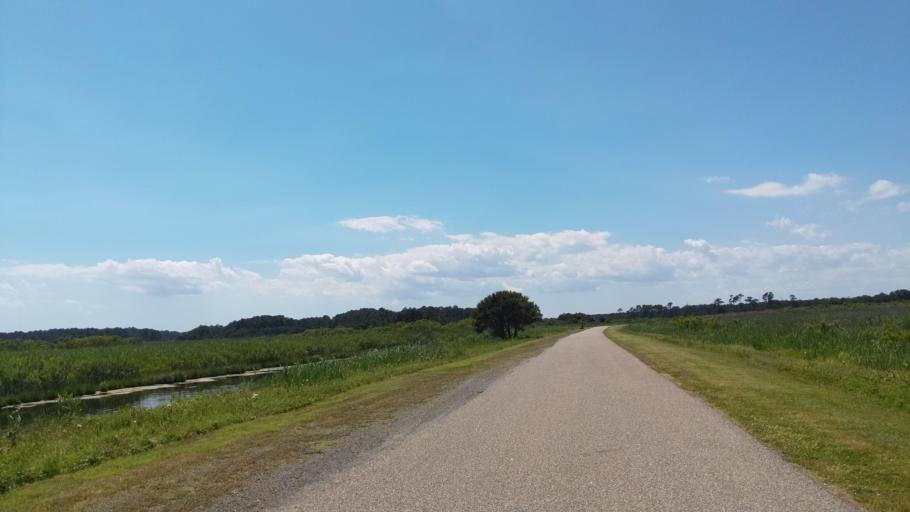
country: US
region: Virginia
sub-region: Accomack County
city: Chincoteague
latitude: 37.9013
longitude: -75.3462
